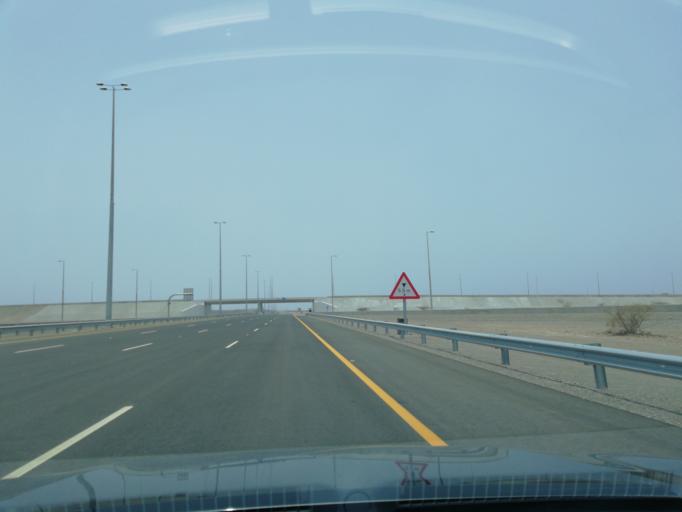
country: OM
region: Al Batinah
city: Al Liwa'
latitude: 24.5273
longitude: 56.5024
